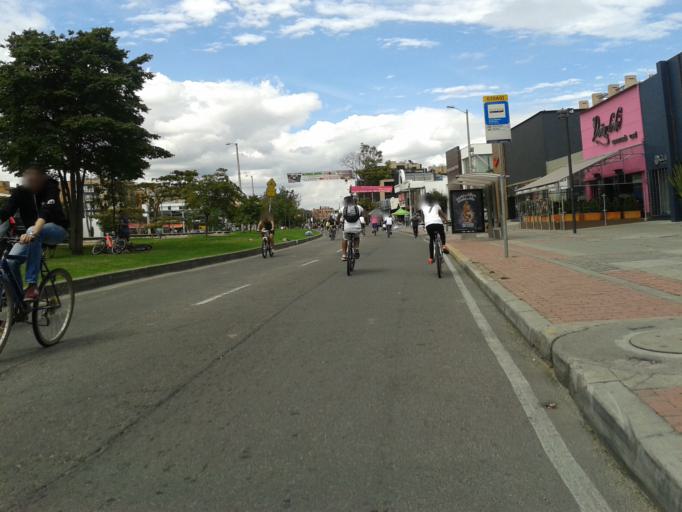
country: CO
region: Bogota D.C.
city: Barrio San Luis
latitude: 4.6970
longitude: -74.0445
